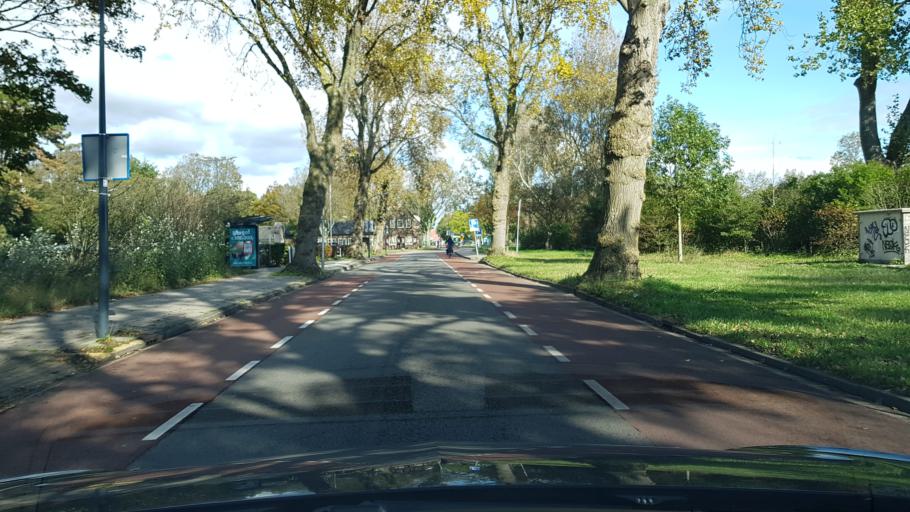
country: NL
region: North Holland
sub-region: Gemeente Velsen
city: Velsen-Zuid
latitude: 52.4215
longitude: 4.6589
